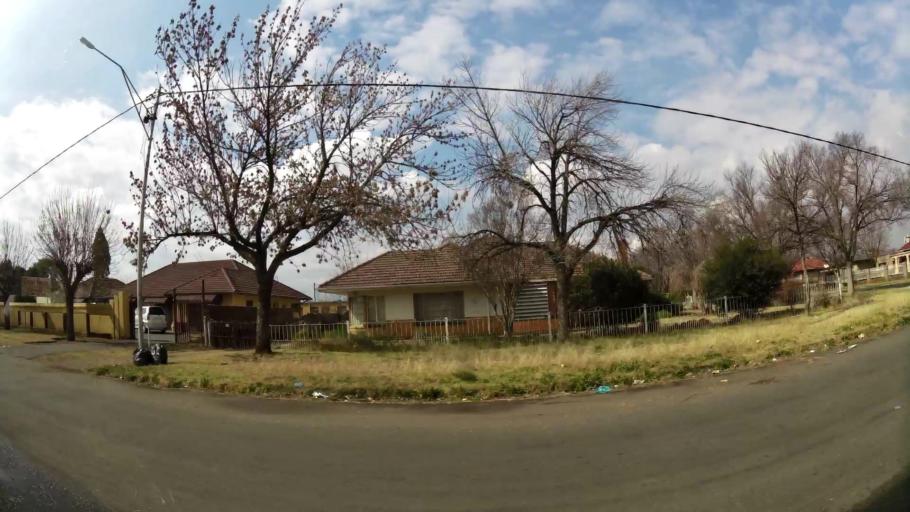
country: ZA
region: Gauteng
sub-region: Sedibeng District Municipality
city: Vereeniging
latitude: -26.6754
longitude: 27.9204
